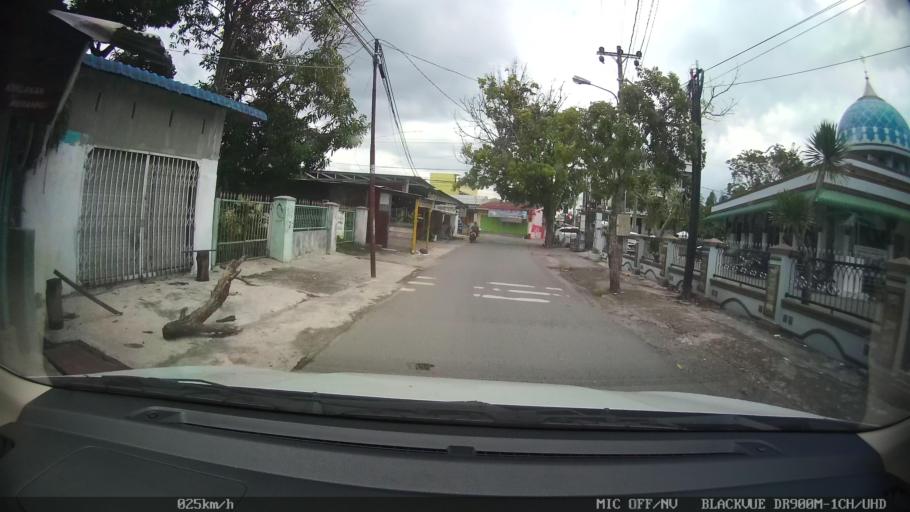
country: ID
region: North Sumatra
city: Medan
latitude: 3.6133
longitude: 98.6459
